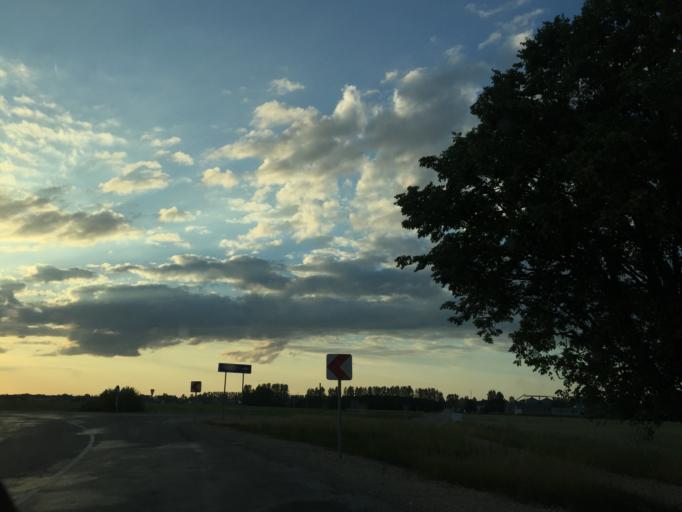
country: LV
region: Sigulda
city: Sigulda
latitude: 57.1367
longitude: 24.8943
